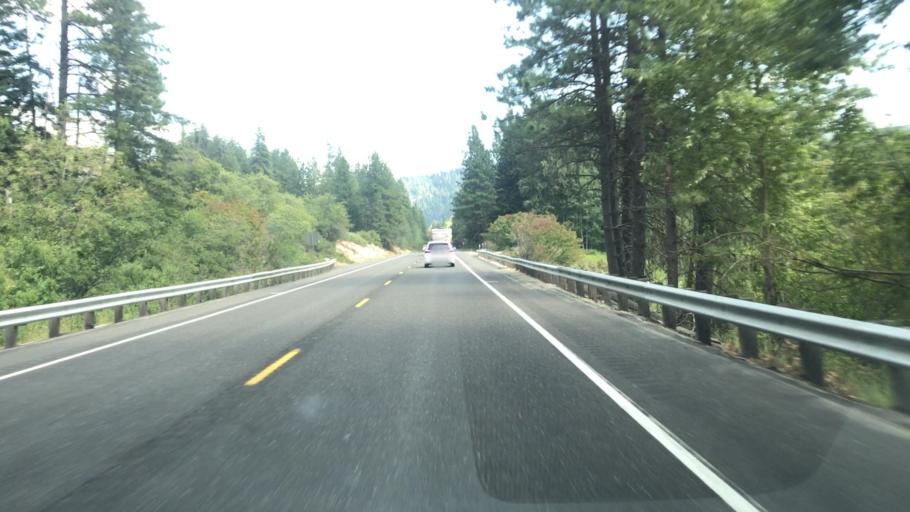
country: US
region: Washington
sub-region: Chelan County
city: Leavenworth
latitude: 47.7748
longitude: -120.8183
